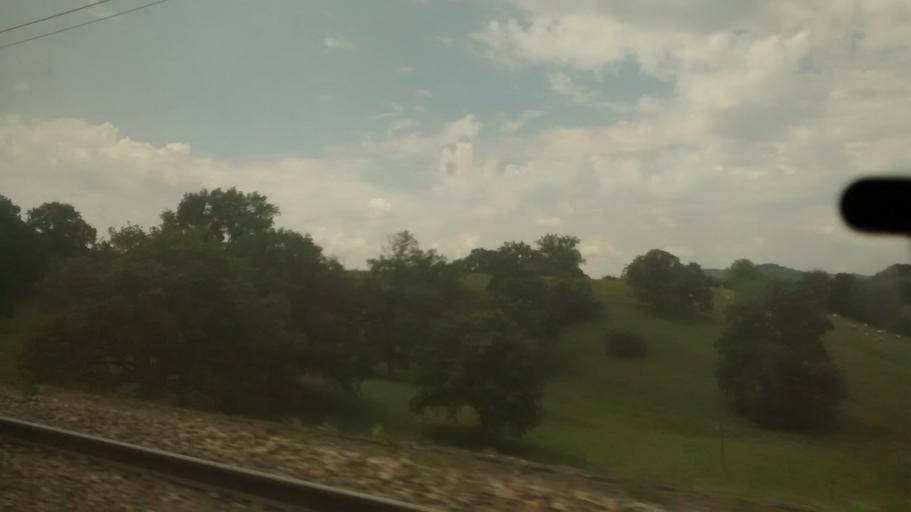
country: FR
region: Bourgogne
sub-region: Departement de Saone-et-Loire
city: Le Breuil
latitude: 46.8301
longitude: 4.4924
